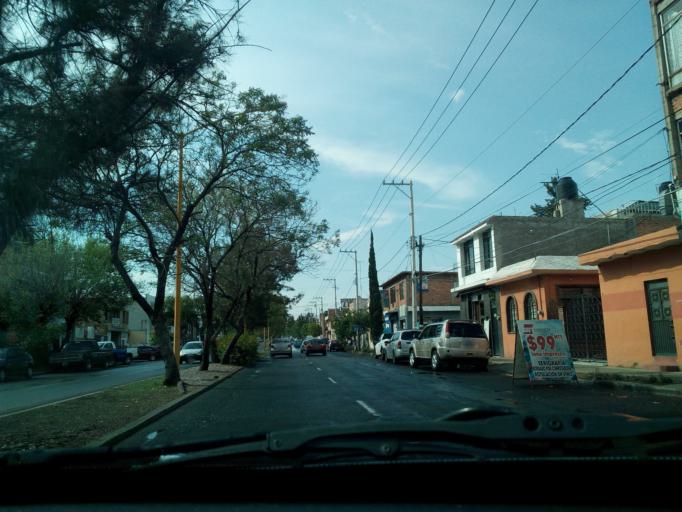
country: MX
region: Aguascalientes
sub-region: Aguascalientes
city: Aguascalientes
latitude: 21.8955
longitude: -102.2954
